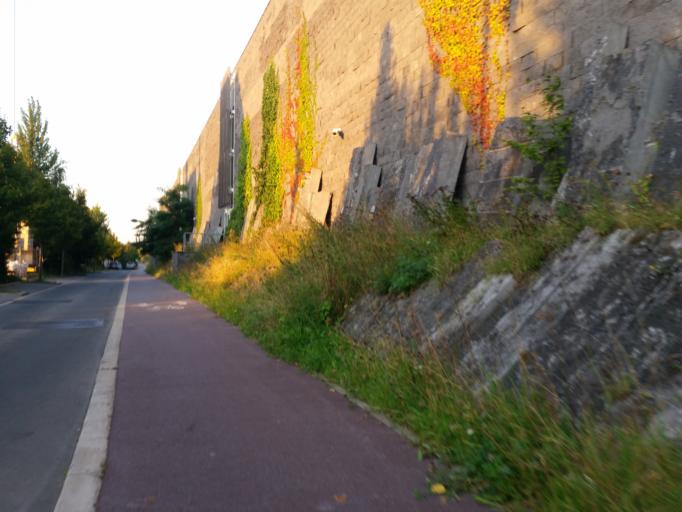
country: BE
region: Flanders
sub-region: Provincie Vlaams-Brabant
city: Diegem
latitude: 50.8861
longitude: 4.4128
